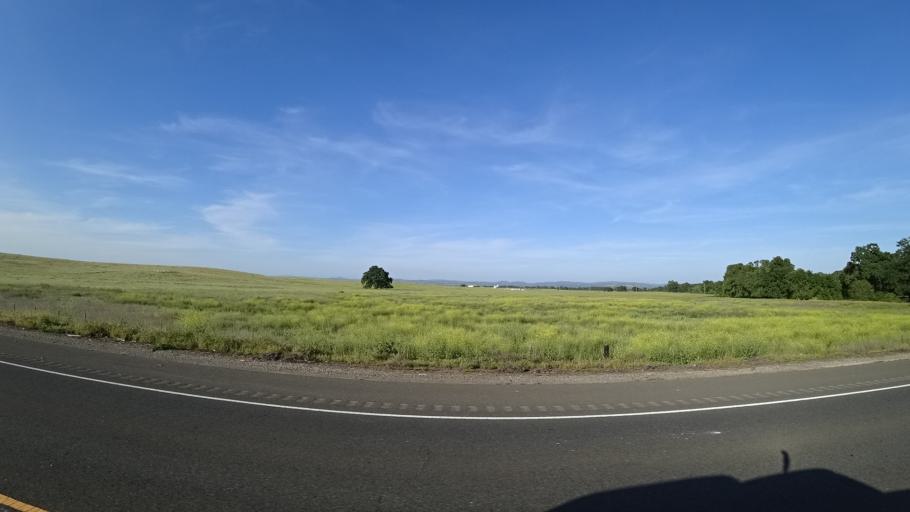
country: US
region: California
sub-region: Placer County
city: Sheridan
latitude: 38.9387
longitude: -121.3519
